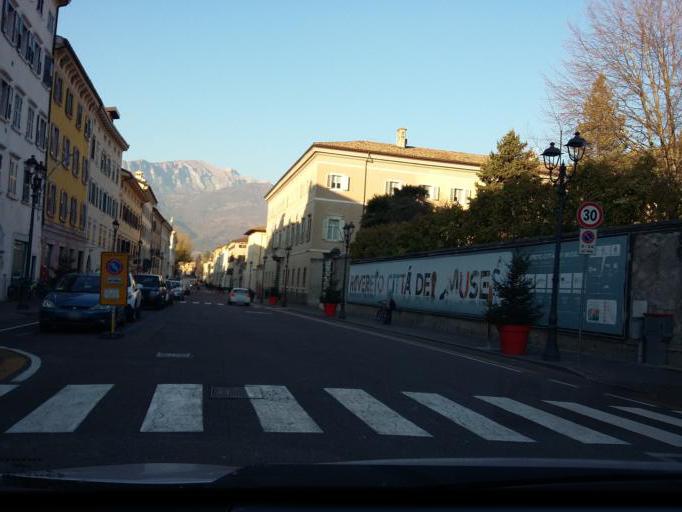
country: IT
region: Trentino-Alto Adige
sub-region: Provincia di Trento
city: Rovereto
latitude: 45.8916
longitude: 11.0438
